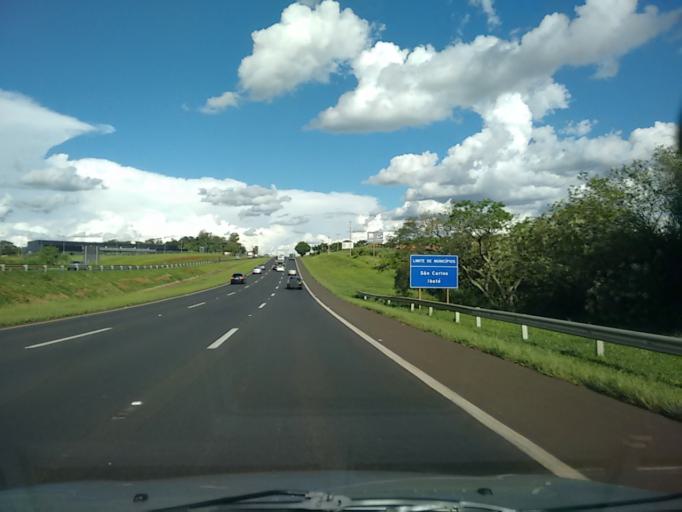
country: BR
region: Sao Paulo
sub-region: Ibate
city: Ibate
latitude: -21.9725
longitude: -47.9455
